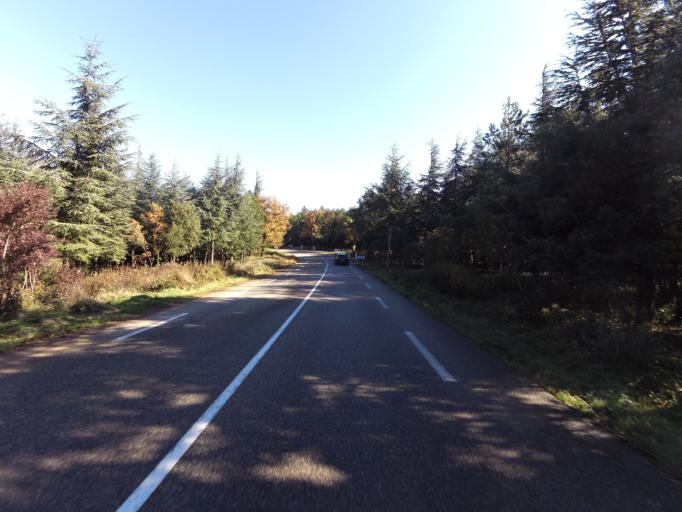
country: FR
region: Rhone-Alpes
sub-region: Departement de l'Ardeche
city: Bourg-Saint-Andeol
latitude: 44.3956
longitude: 4.5902
